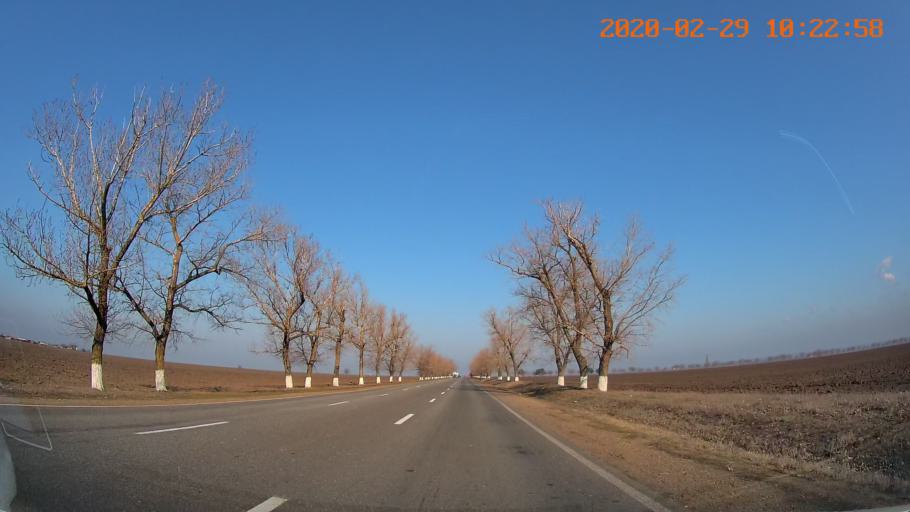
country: MD
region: Telenesti
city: Tiraspolul Nou
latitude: 46.8812
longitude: 29.6044
